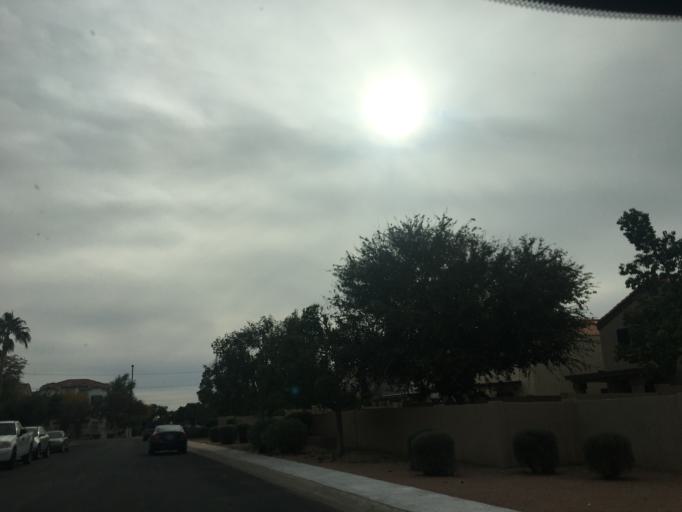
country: US
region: Arizona
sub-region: Maricopa County
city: Gilbert
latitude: 33.3609
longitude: -111.7938
